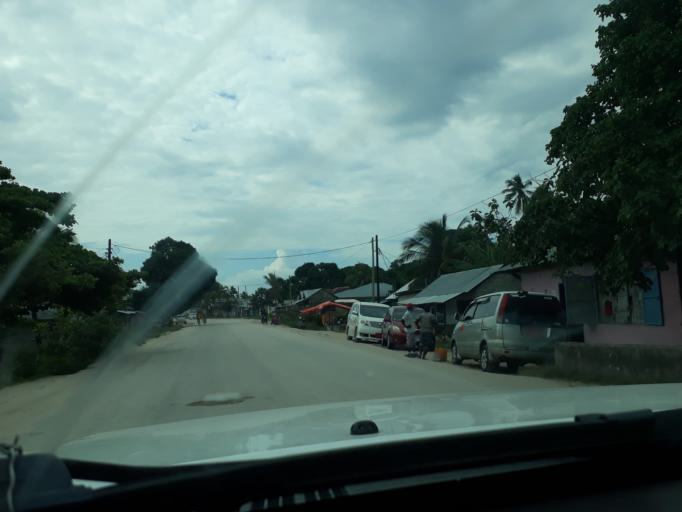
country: TZ
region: Zanzibar Central/South
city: Koani
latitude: -6.0852
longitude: 39.2227
